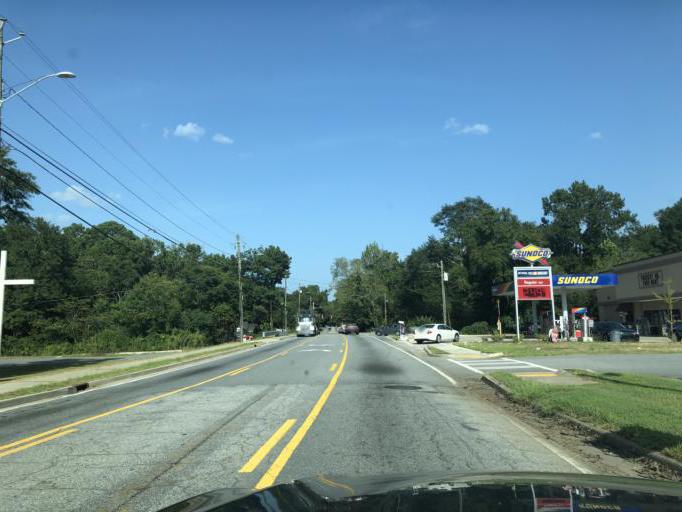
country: US
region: Georgia
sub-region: Muscogee County
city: Columbus
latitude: 32.4840
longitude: -84.9236
